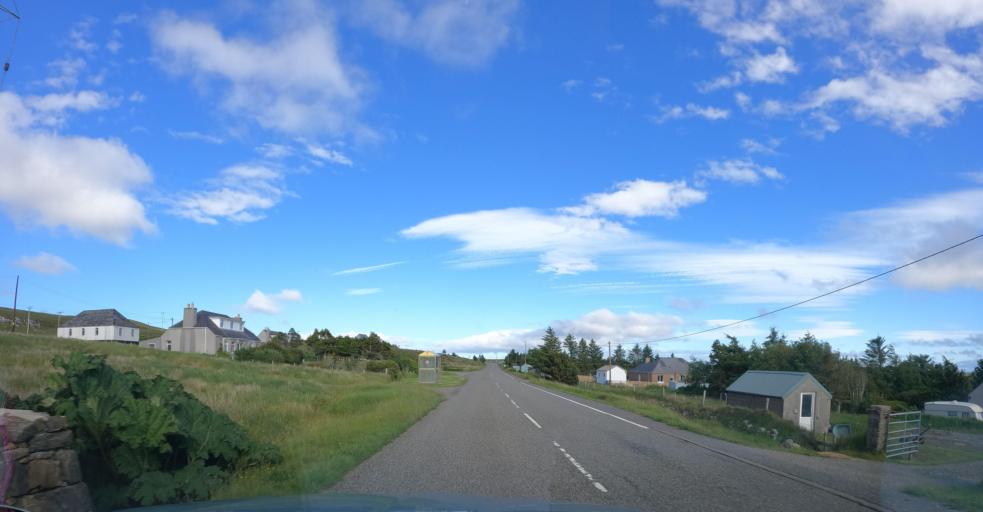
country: GB
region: Scotland
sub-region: Eilean Siar
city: Stornoway
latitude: 58.1719
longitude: -6.5791
